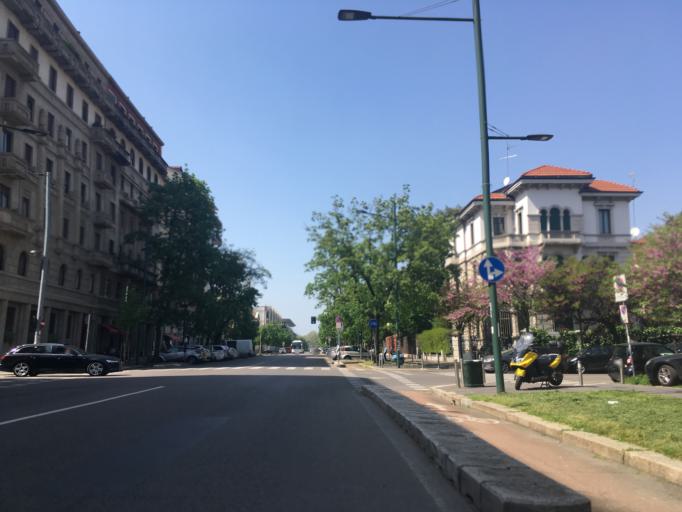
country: IT
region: Lombardy
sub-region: Citta metropolitana di Milano
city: Milano
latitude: 45.4751
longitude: 9.1493
